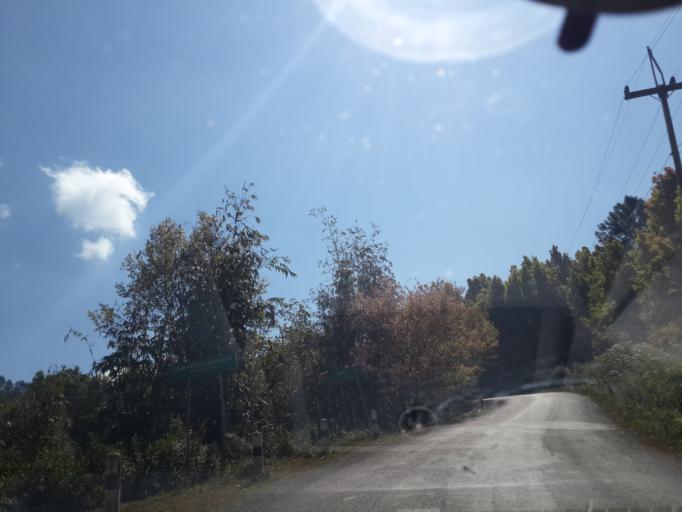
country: TH
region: Chiang Mai
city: Fang
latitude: 19.9175
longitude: 99.0495
